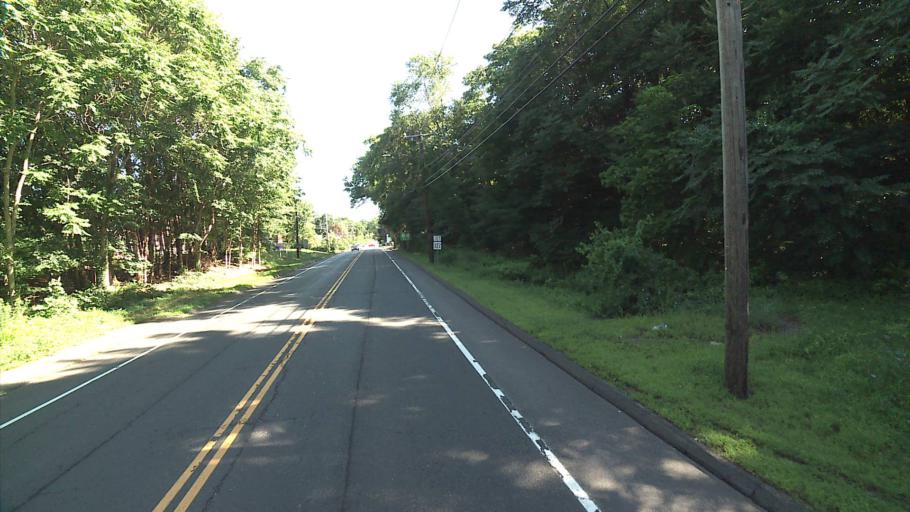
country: US
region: Connecticut
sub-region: New Haven County
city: Cheshire Village
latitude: 41.5614
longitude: -72.8902
